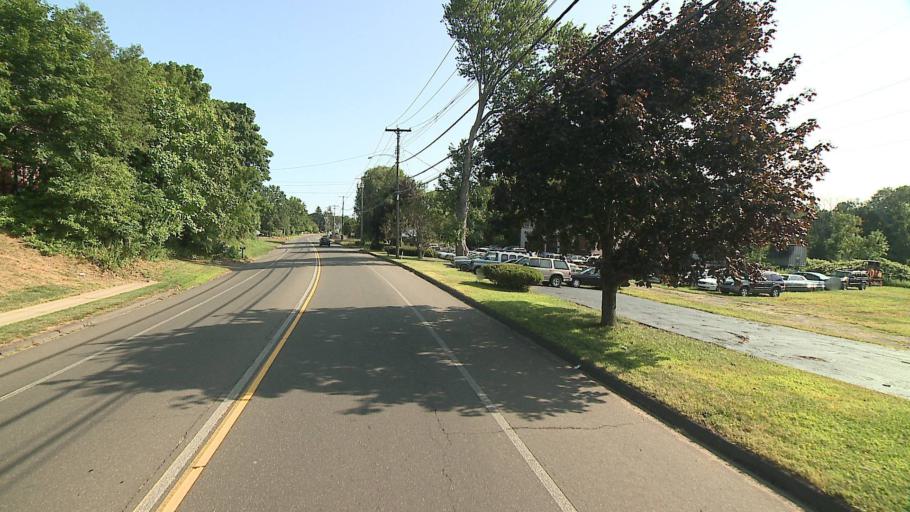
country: US
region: Connecticut
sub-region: New Haven County
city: North Haven
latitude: 41.3840
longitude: -72.8749
